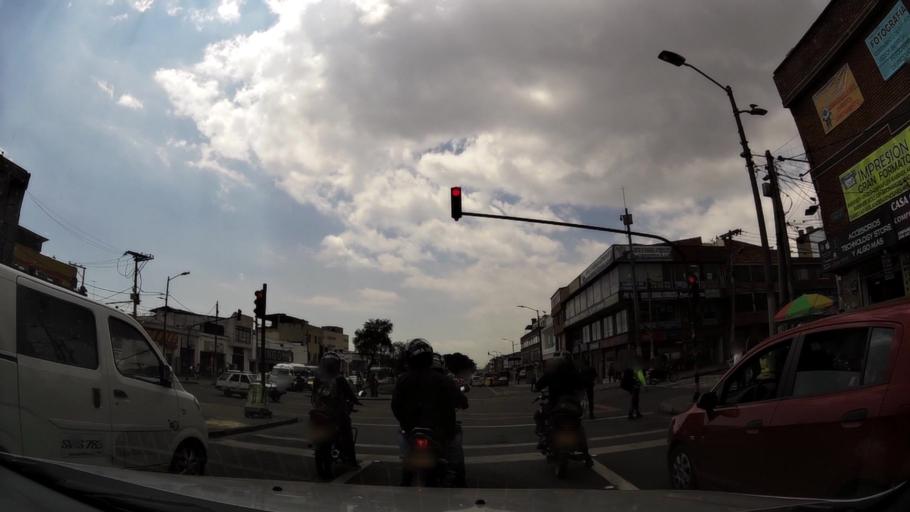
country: CO
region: Bogota D.C.
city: Bogota
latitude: 4.5825
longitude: -74.1035
